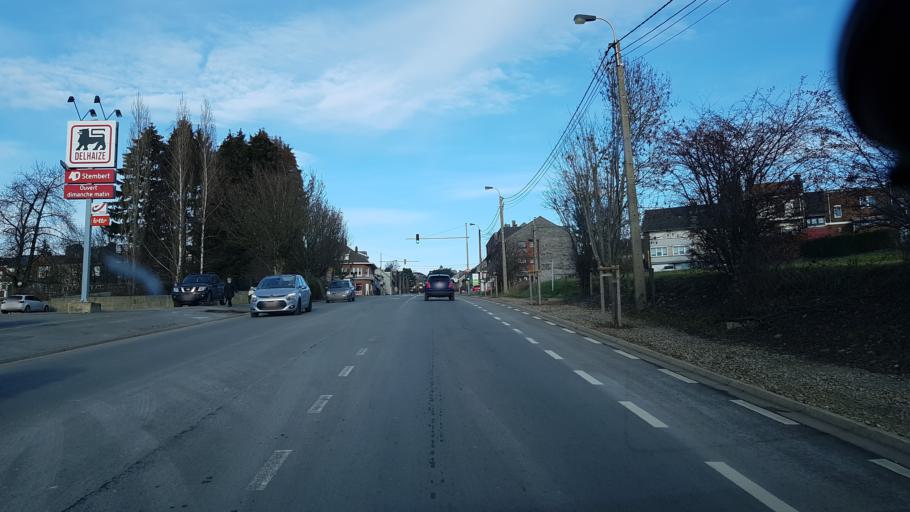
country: BE
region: Wallonia
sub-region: Province de Liege
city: Verviers
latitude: 50.5870
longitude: 5.8880
